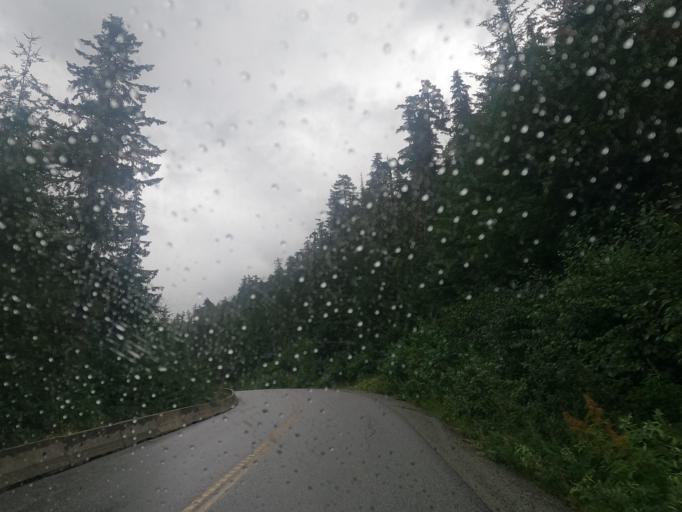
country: CA
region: British Columbia
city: Pemberton
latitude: 50.3375
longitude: -122.5420
